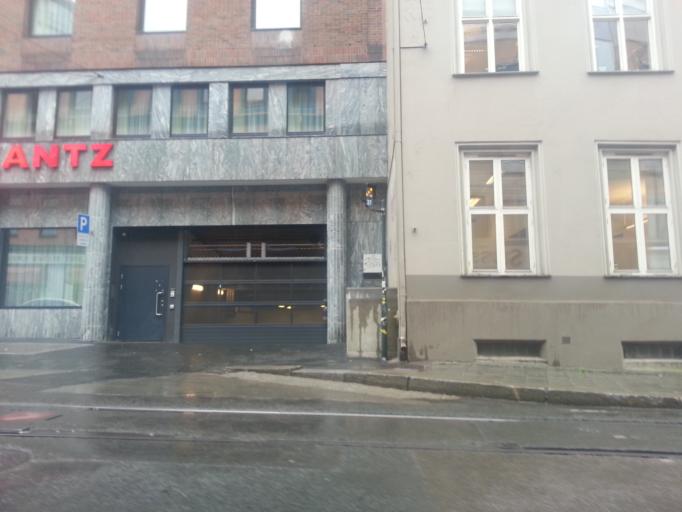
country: NO
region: Oslo
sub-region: Oslo
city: Oslo
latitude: 59.9160
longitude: 10.7403
